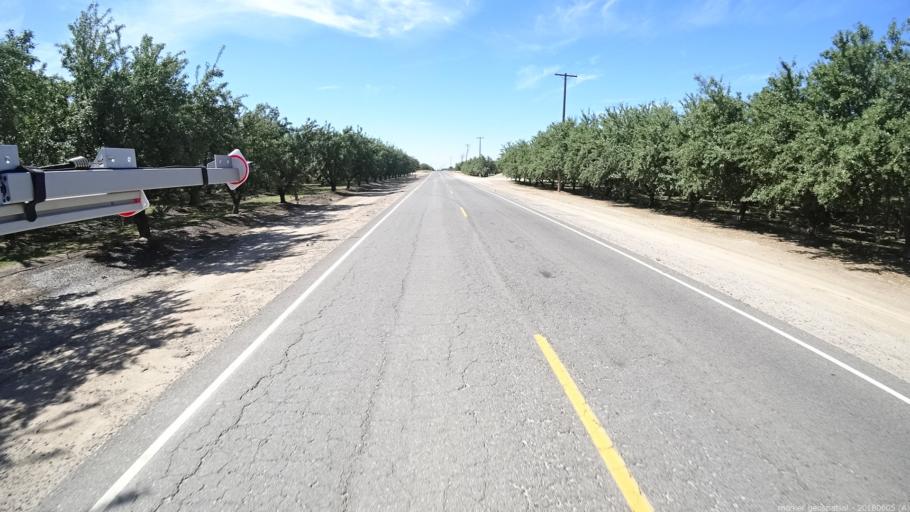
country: US
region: California
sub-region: Madera County
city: Chowchilla
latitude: 37.0802
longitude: -120.3828
